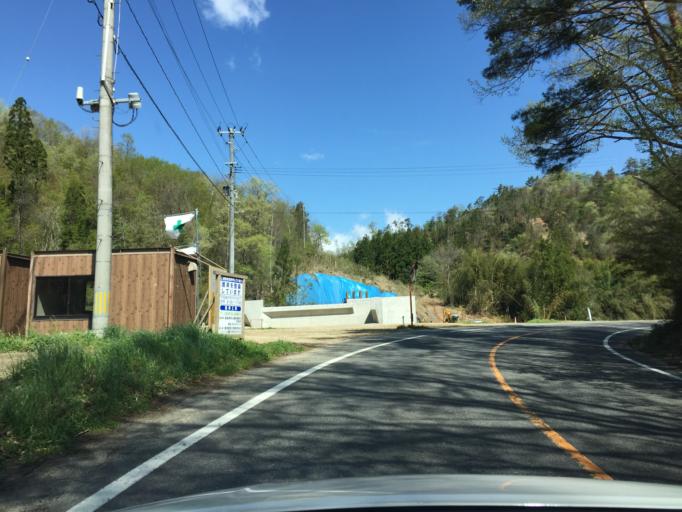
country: JP
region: Fukushima
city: Funehikimachi-funehiki
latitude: 37.5350
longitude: 140.5402
